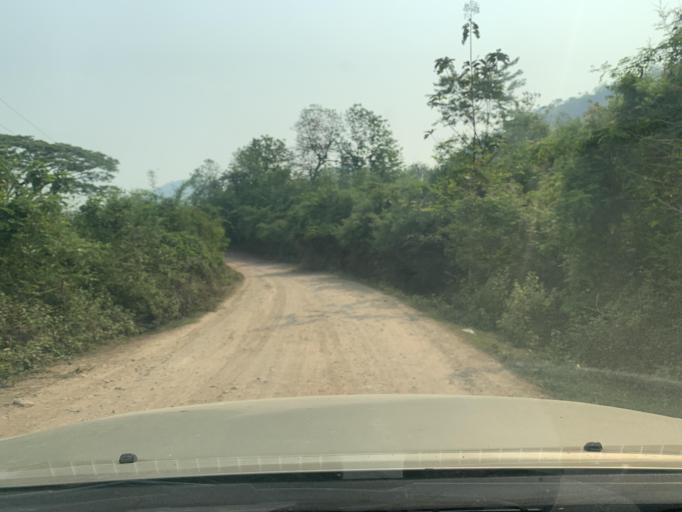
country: LA
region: Louangphabang
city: Louangphabang
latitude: 19.9077
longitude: 102.1320
